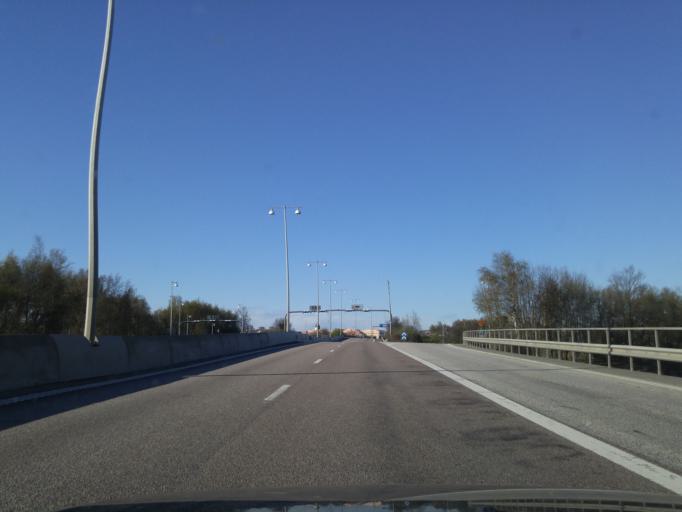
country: SE
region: Vaestra Goetaland
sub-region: Goteborg
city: Goeteborg
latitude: 57.7213
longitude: 11.9954
